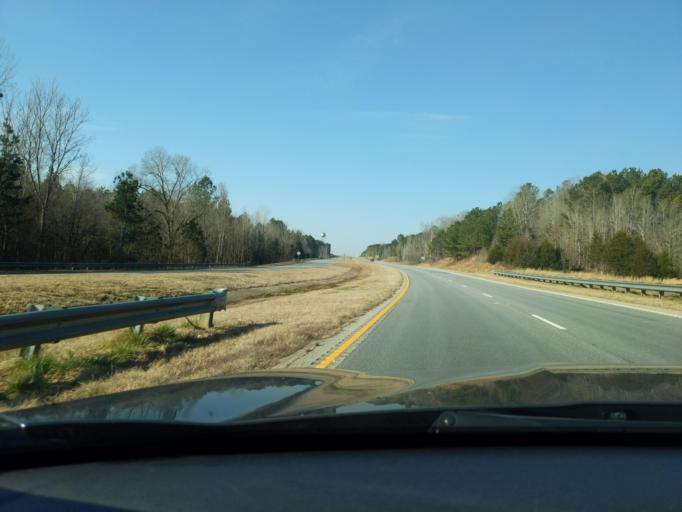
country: US
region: South Carolina
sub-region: Abbeville County
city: Calhoun Falls
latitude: 34.1105
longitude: -82.5129
